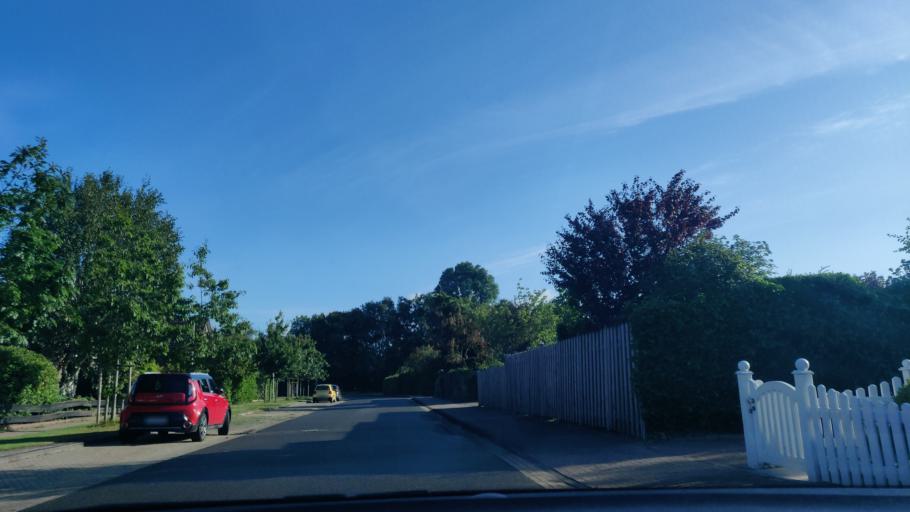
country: DE
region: Lower Saxony
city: Cuxhaven
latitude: 53.8786
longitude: 8.6775
